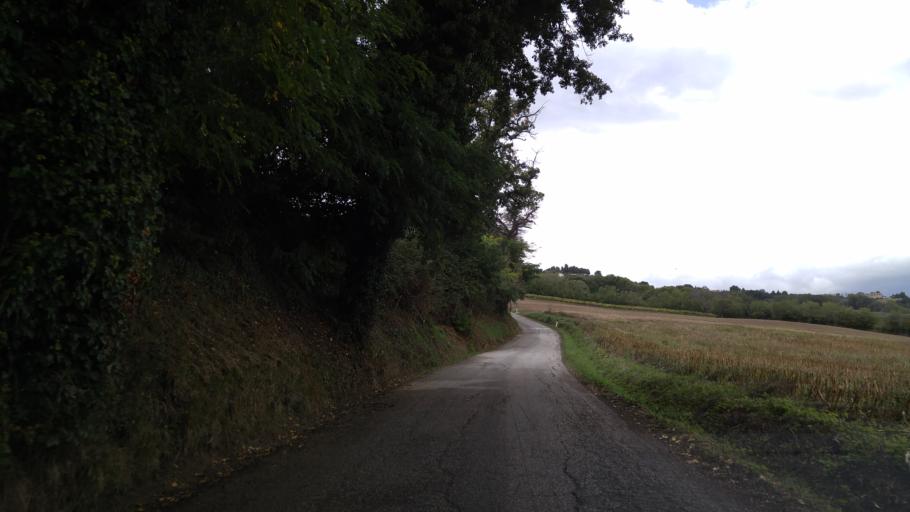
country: IT
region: The Marches
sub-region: Provincia di Pesaro e Urbino
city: Cartoceto
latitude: 43.7873
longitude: 12.8850
